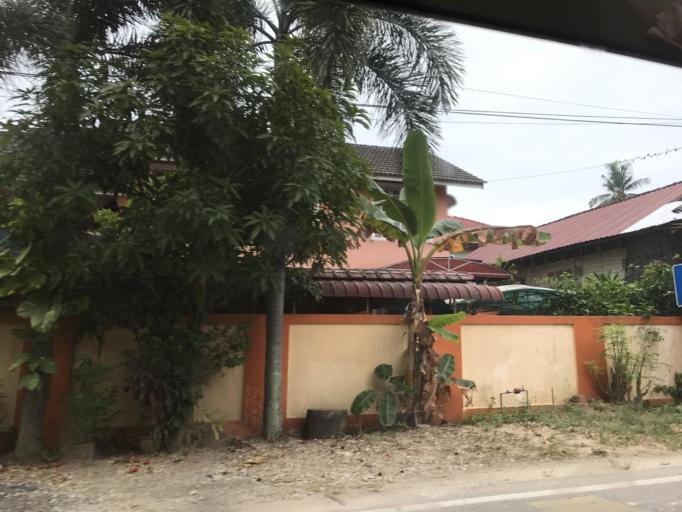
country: MY
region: Kelantan
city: Kota Bharu
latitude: 6.1441
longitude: 102.2256
